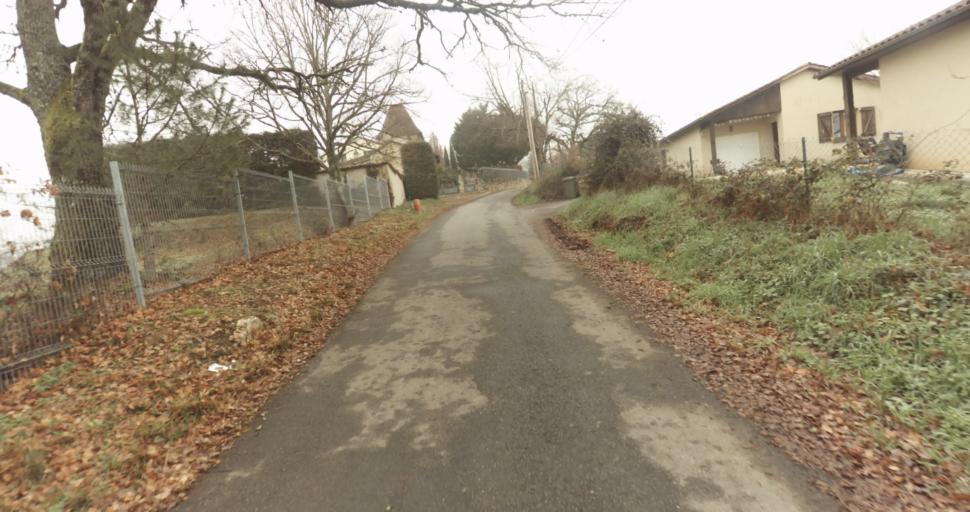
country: FR
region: Midi-Pyrenees
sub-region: Departement du Lot
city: Figeac
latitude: 44.6213
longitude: 2.0368
